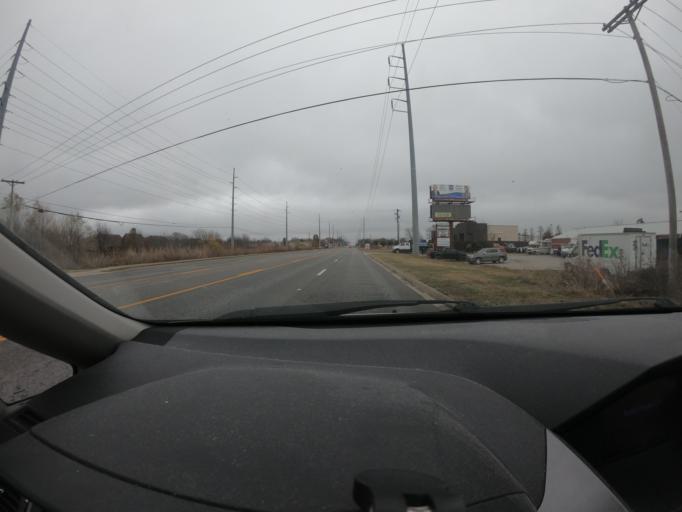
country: US
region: Arkansas
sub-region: Benton County
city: Bentonville
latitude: 36.3576
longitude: -94.2450
